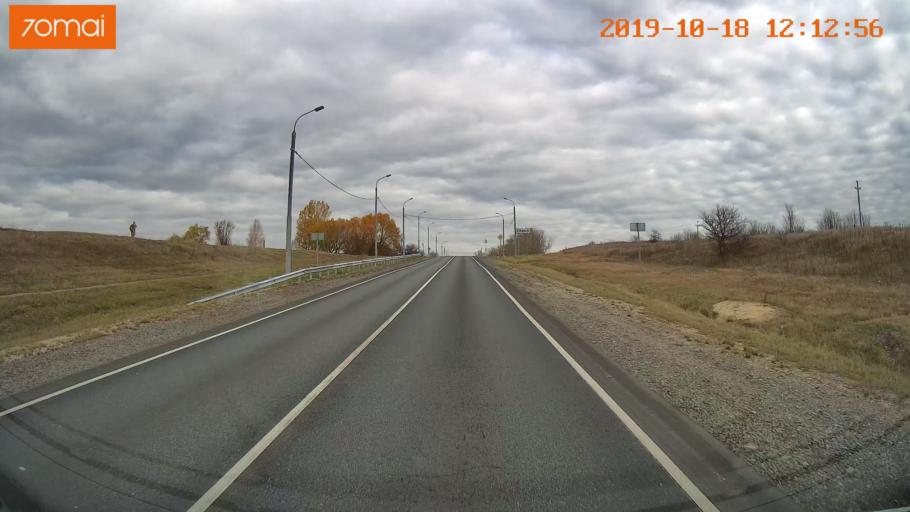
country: RU
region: Rjazan
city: Zakharovo
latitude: 54.4170
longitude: 39.3648
